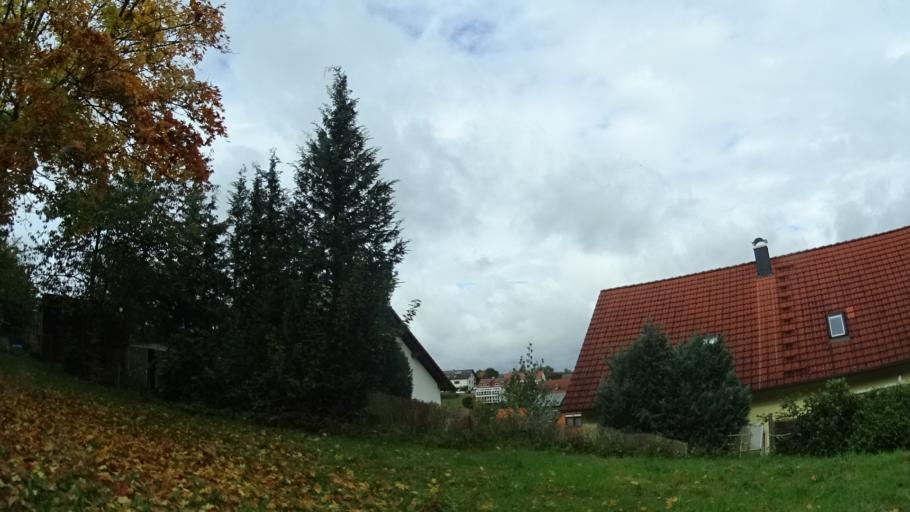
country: DE
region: Bavaria
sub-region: Upper Franconia
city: Viereth-Trunstadt
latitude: 49.9247
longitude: 10.7435
